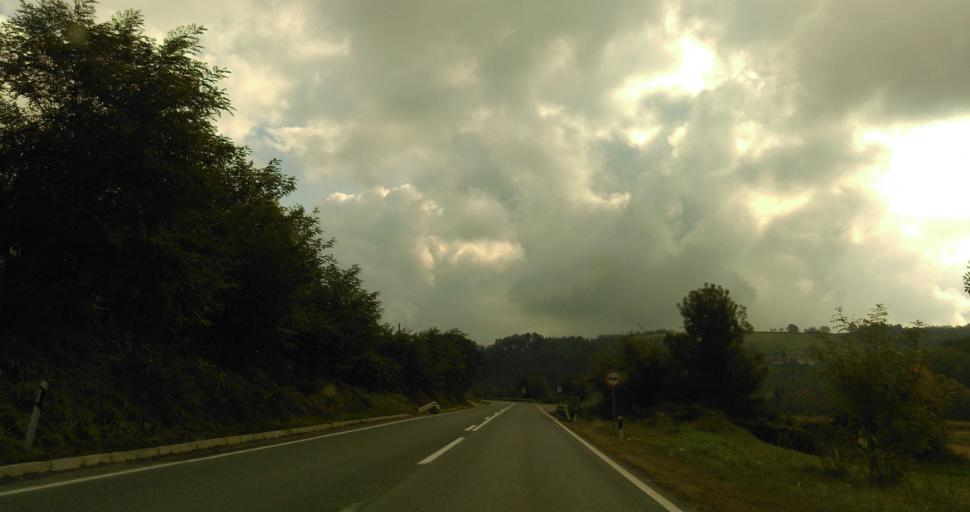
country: RS
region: Central Serbia
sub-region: Kolubarski Okrug
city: Ljig
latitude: 44.1957
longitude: 20.2915
